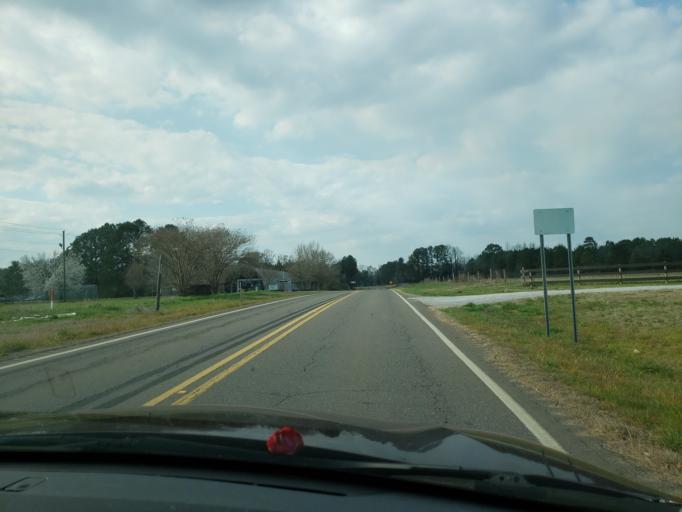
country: US
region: Alabama
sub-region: Hale County
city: Greensboro
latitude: 32.7175
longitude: -87.6198
